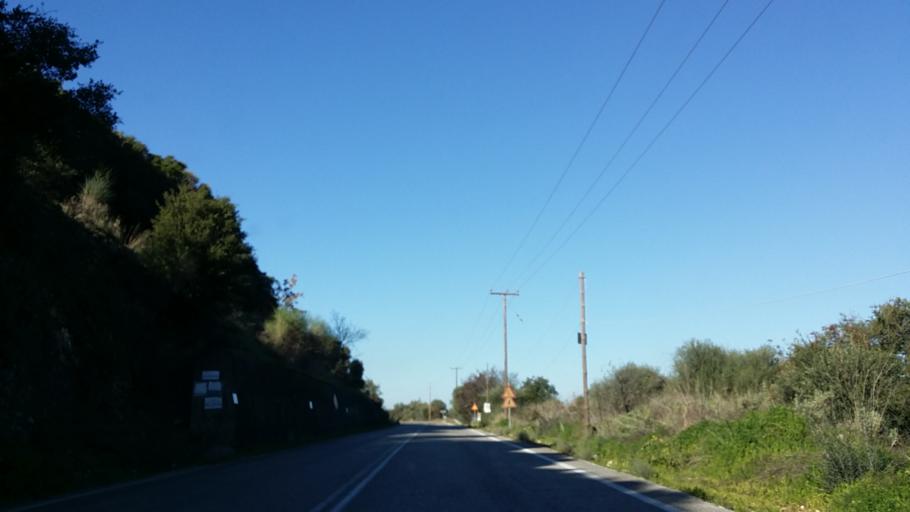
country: GR
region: West Greece
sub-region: Nomos Aitolias kai Akarnanias
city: Amfilochia
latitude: 38.8645
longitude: 21.0766
